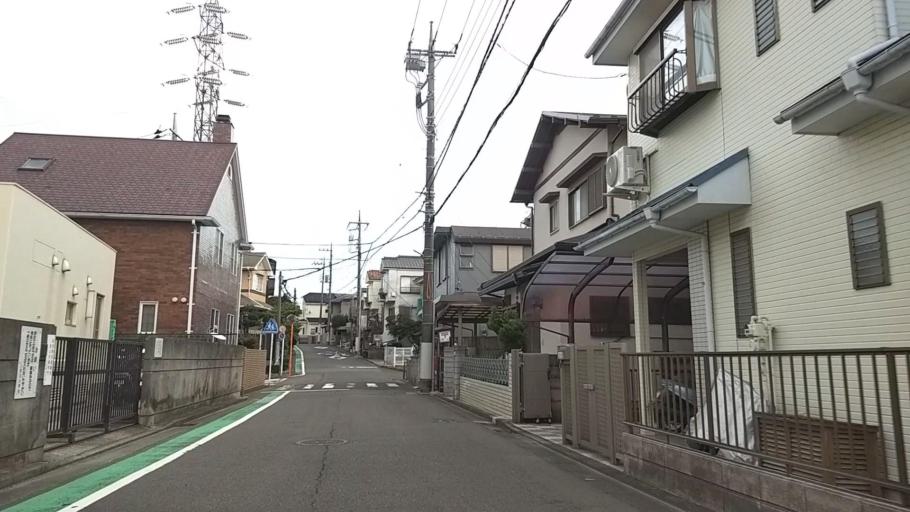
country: JP
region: Kanagawa
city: Yokohama
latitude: 35.4835
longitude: 139.5661
